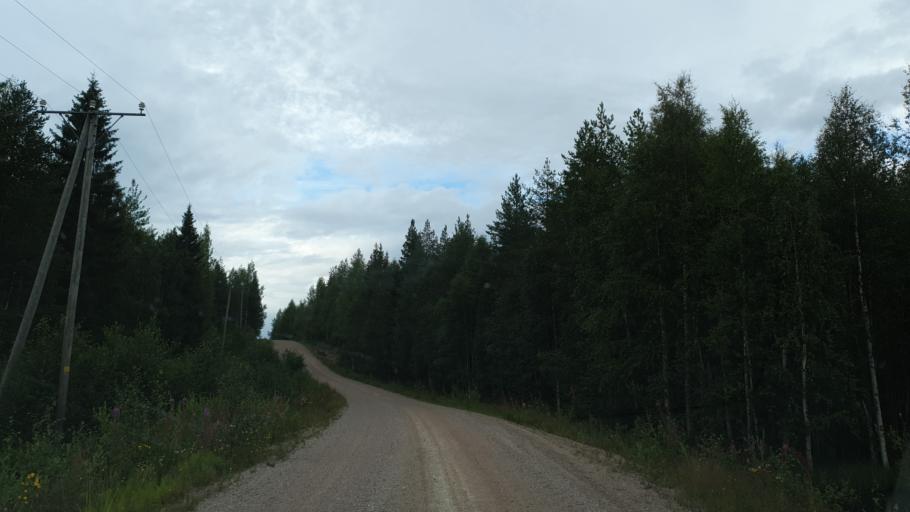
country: FI
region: Kainuu
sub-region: Kehys-Kainuu
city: Suomussalmi
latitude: 64.4521
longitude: 28.9743
